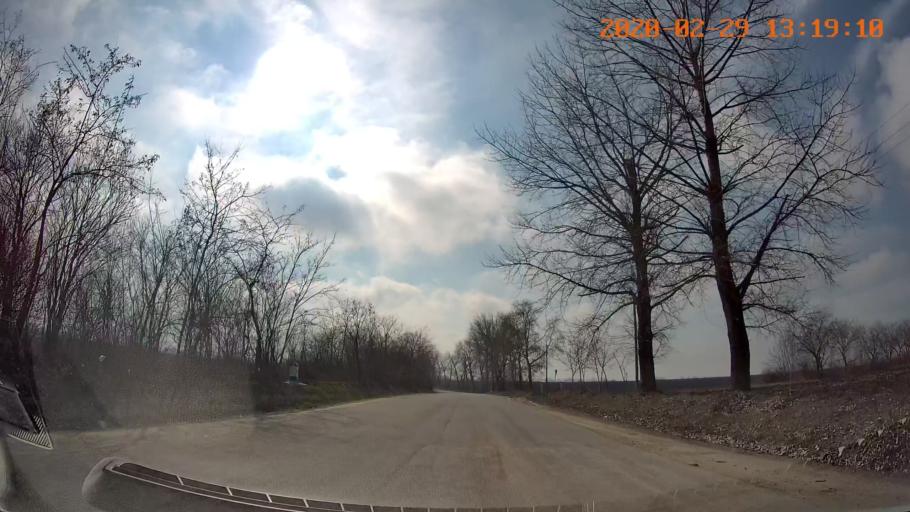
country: MD
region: Telenesti
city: Camenca
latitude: 47.9907
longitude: 28.6532
